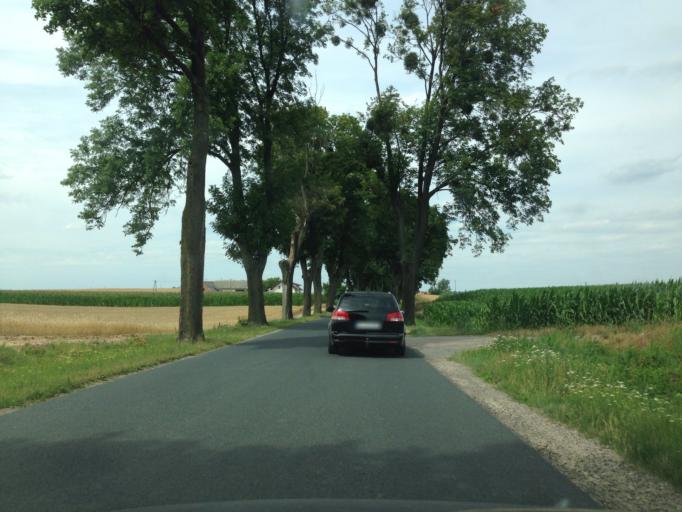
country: PL
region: Kujawsko-Pomorskie
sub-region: Powiat brodnicki
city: Brodnica
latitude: 53.3091
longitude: 19.3917
